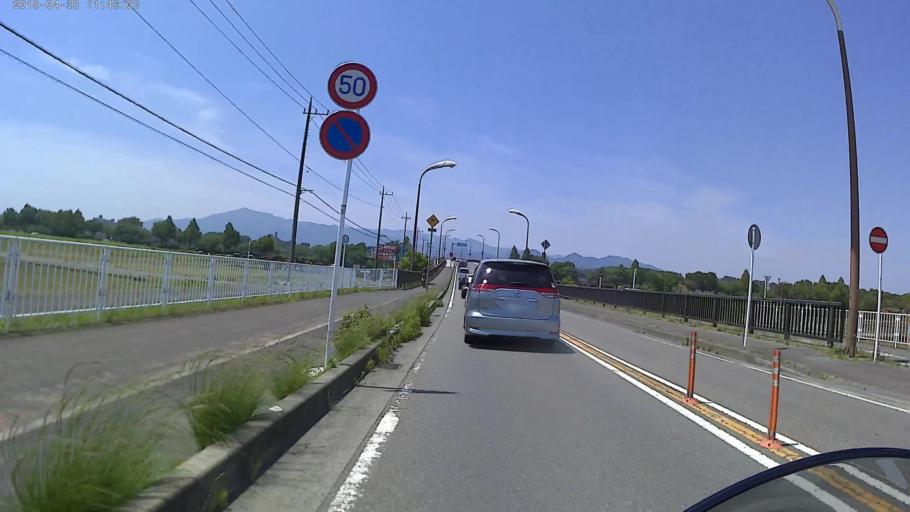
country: JP
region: Kanagawa
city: Zama
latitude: 35.4865
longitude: 139.3798
